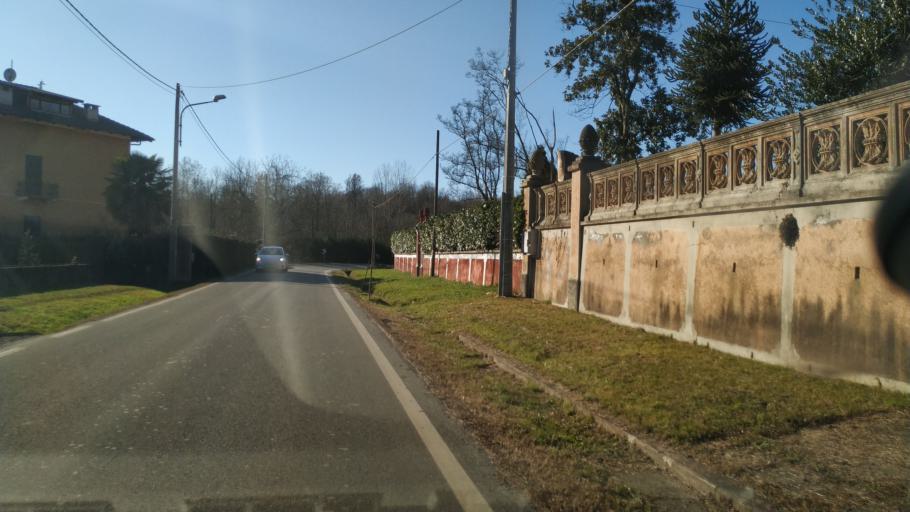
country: IT
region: Piedmont
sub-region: Provincia di Biella
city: Brusnengo
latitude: 45.5915
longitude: 8.2686
